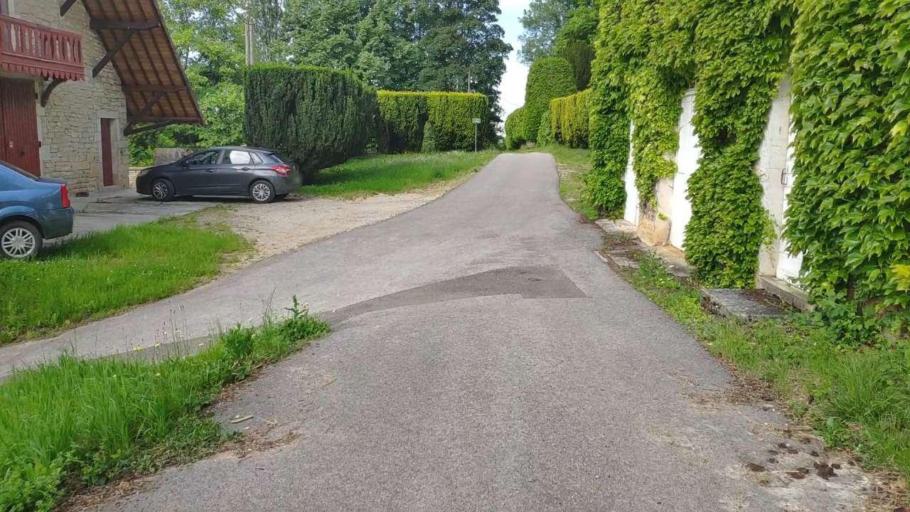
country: FR
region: Franche-Comte
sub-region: Departement du Jura
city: Perrigny
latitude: 46.7714
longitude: 5.6066
